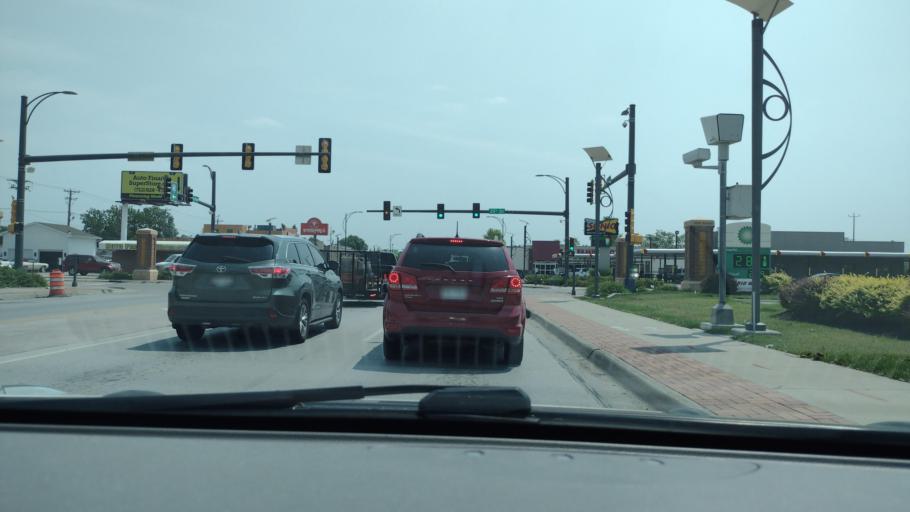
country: US
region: Iowa
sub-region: Pottawattamie County
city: Carter Lake
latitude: 41.2619
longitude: -95.9026
